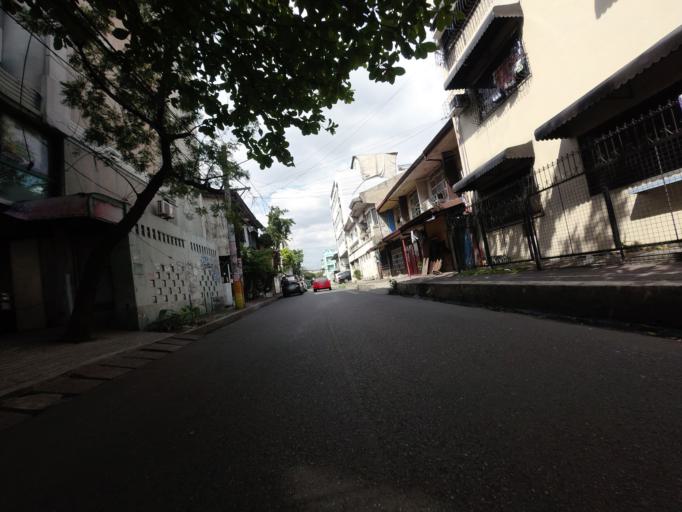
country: PH
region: Metro Manila
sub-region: City of Manila
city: Quiapo
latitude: 14.5728
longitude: 121.0010
